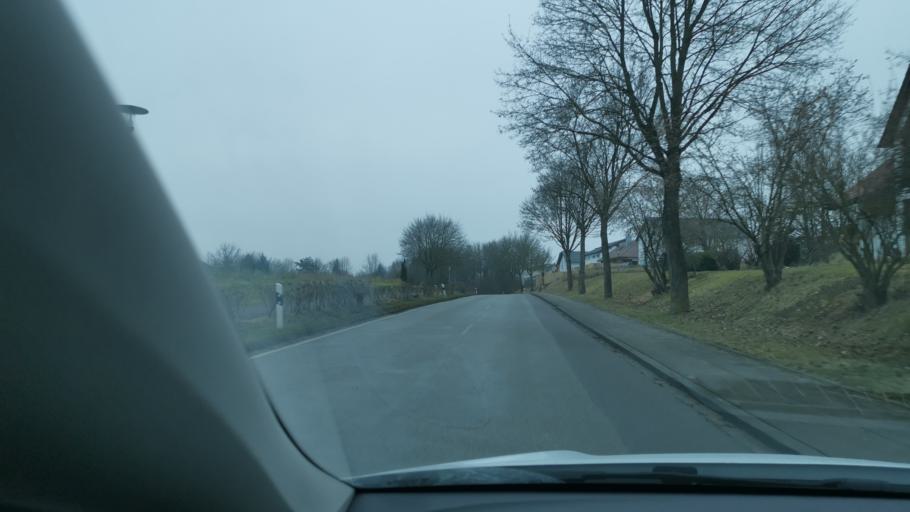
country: DE
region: Bavaria
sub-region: Swabia
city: Holzheim
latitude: 48.5872
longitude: 10.9610
